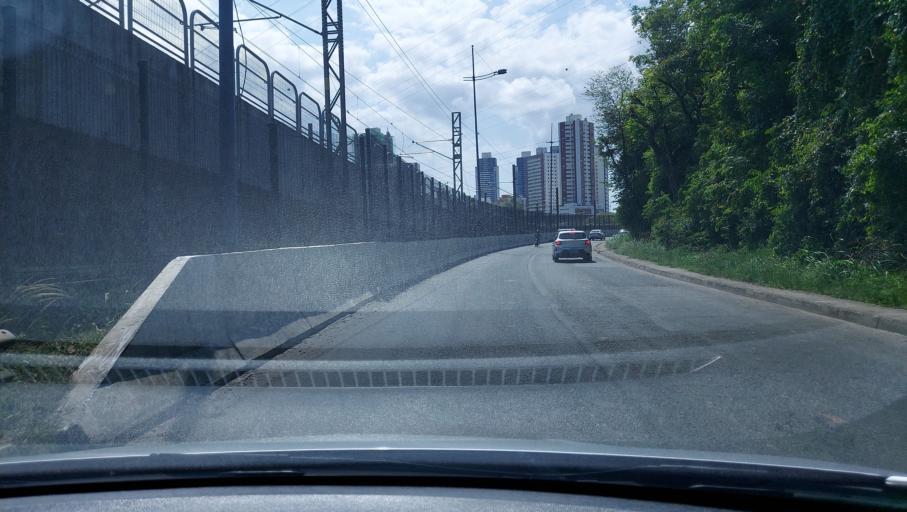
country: BR
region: Bahia
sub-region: Salvador
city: Salvador
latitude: -12.9767
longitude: -38.4744
